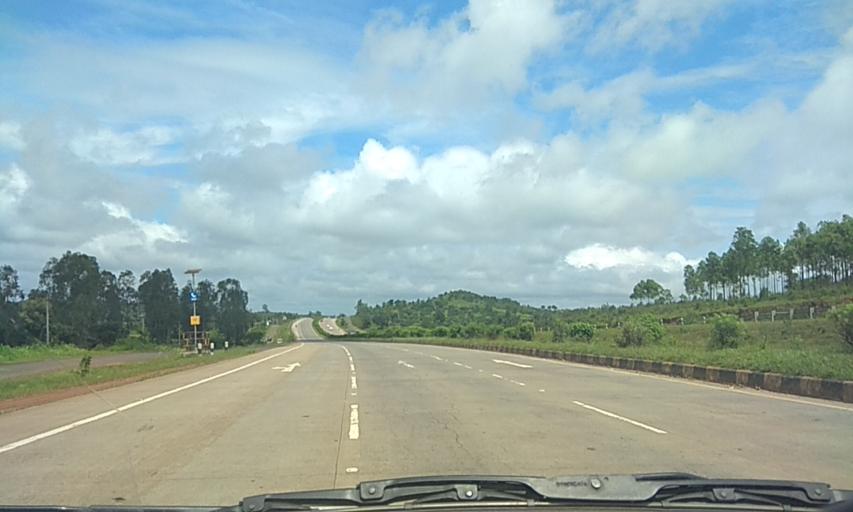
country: IN
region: Karnataka
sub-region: Dharwad
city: Alnavar
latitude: 15.6109
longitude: 74.7668
